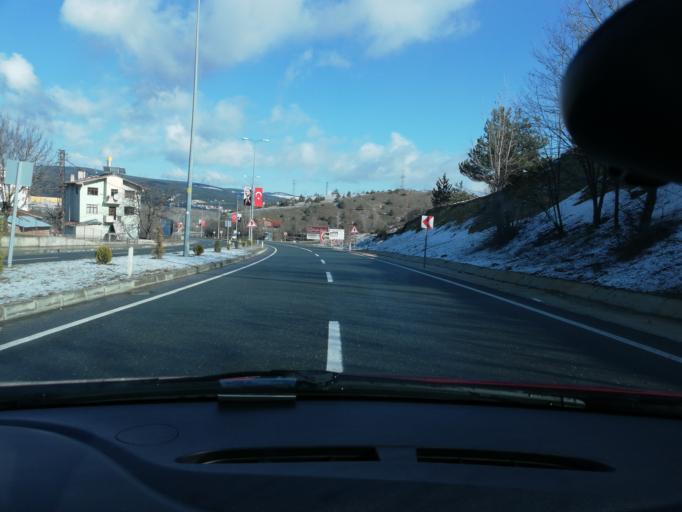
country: TR
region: Kastamonu
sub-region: Cide
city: Kastamonu
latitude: 41.3446
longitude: 33.7672
